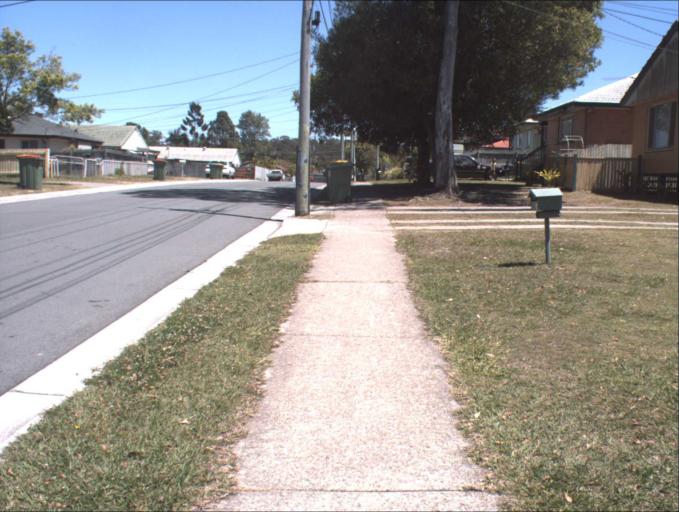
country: AU
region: Queensland
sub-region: Logan
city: Woodridge
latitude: -27.6310
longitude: 153.1055
